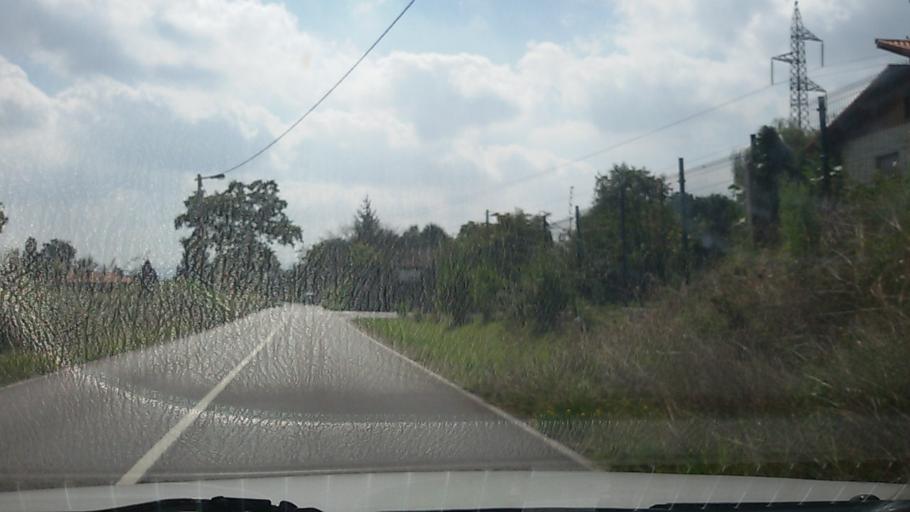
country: ES
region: Asturias
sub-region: Province of Asturias
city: Lugones
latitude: 43.4319
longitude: -5.8053
